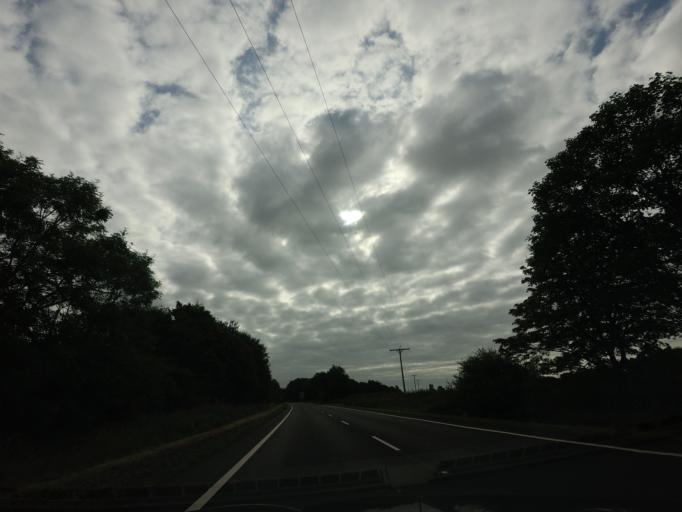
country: GB
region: Scotland
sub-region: Dumfries and Galloway
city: Annan
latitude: 54.9956
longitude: -3.2827
